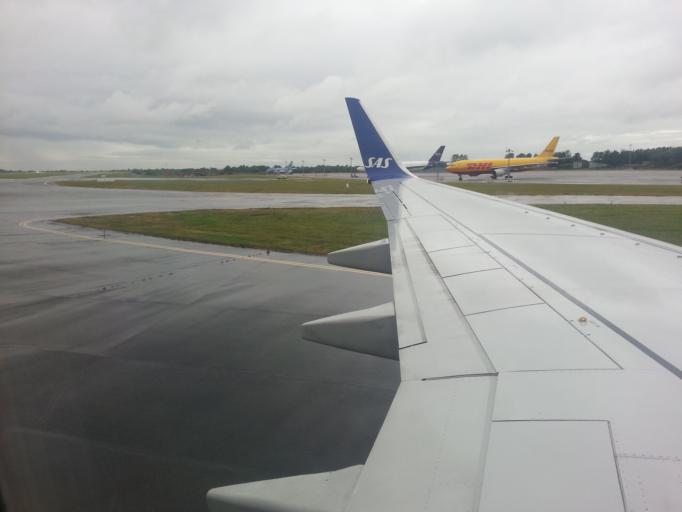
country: IE
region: Leinster
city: Ballymun
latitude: 53.4229
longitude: -6.2593
